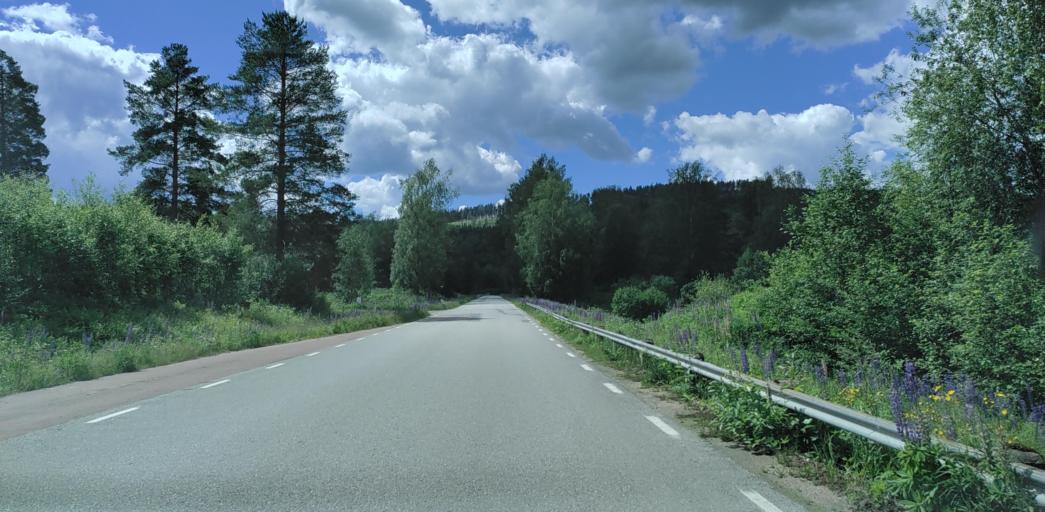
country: SE
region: Vaermland
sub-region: Hagfors Kommun
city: Ekshaerad
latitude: 60.0698
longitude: 13.4826
